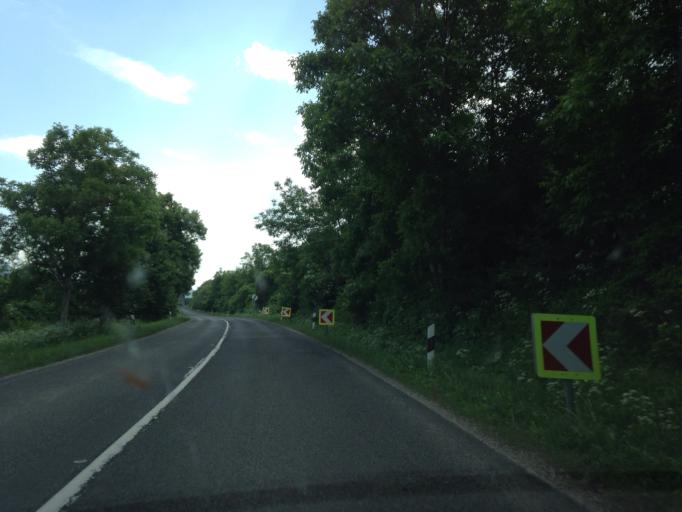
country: HU
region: Komarom-Esztergom
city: Pilismarot
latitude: 47.7988
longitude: 18.8585
